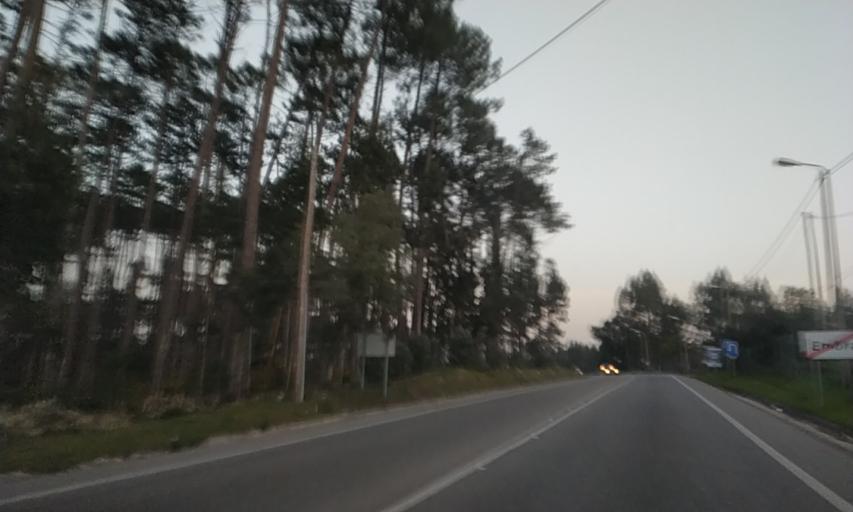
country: PT
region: Leiria
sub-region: Marinha Grande
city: Marinha Grande
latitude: 39.7478
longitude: -8.9078
